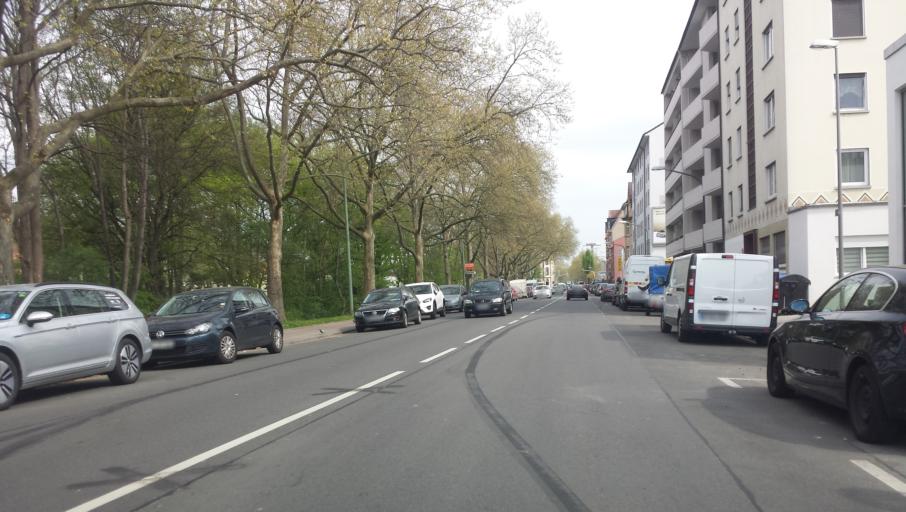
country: DE
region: Rheinland-Pfalz
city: Ludwigshafen am Rhein
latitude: 49.4855
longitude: 8.4272
